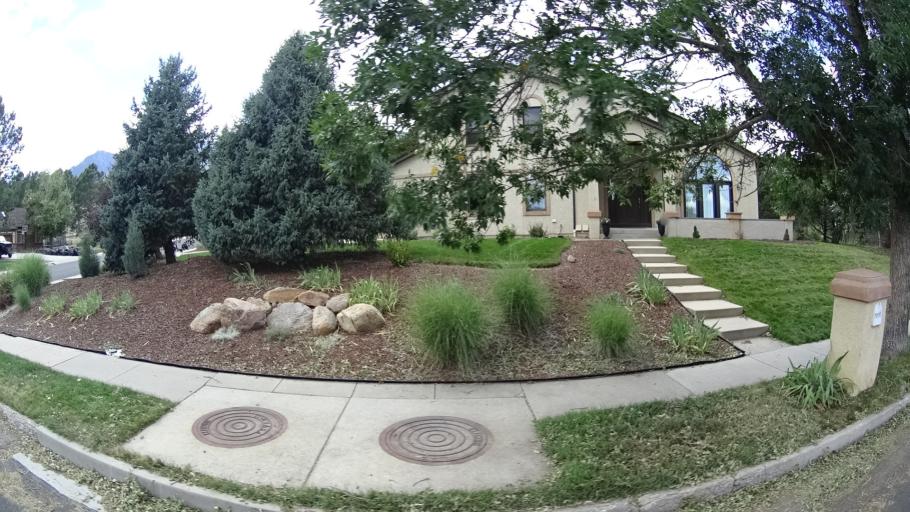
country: US
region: Colorado
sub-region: El Paso County
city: Stratmoor
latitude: 38.7769
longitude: -104.8311
